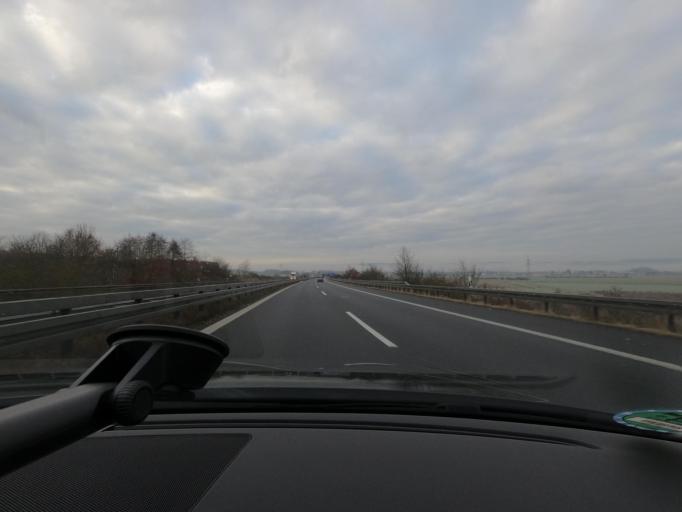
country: DE
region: Bavaria
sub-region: Upper Franconia
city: Ebensfeld
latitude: 50.0674
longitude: 10.9842
